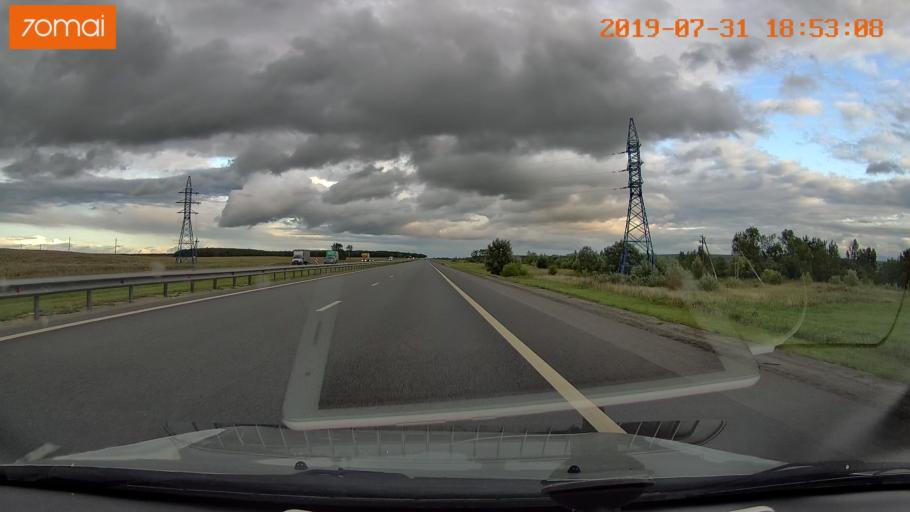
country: RU
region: Moskovskaya
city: Raduzhnyy
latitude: 55.2062
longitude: 38.6470
